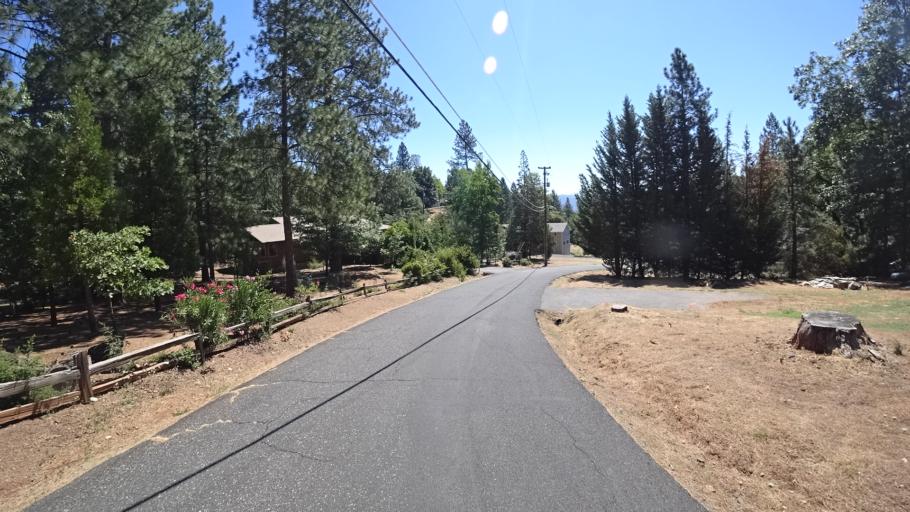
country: US
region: California
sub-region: Calaveras County
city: Forest Meadows
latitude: 38.1867
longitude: -120.3665
